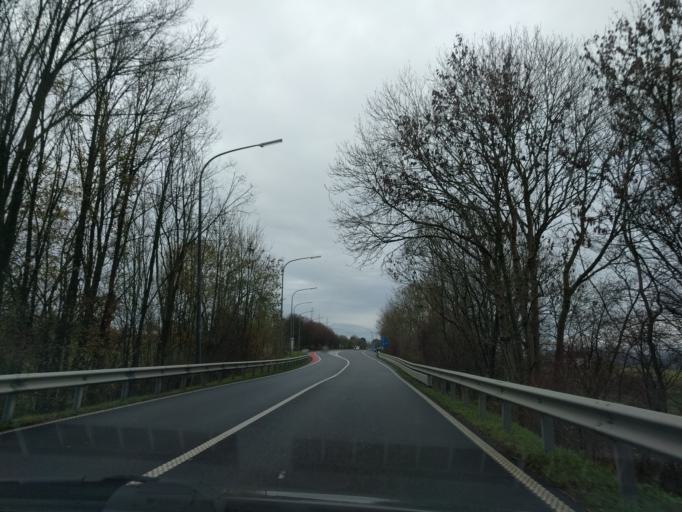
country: BE
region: Wallonia
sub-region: Province de Namur
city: Philippeville
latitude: 50.2021
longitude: 4.5664
